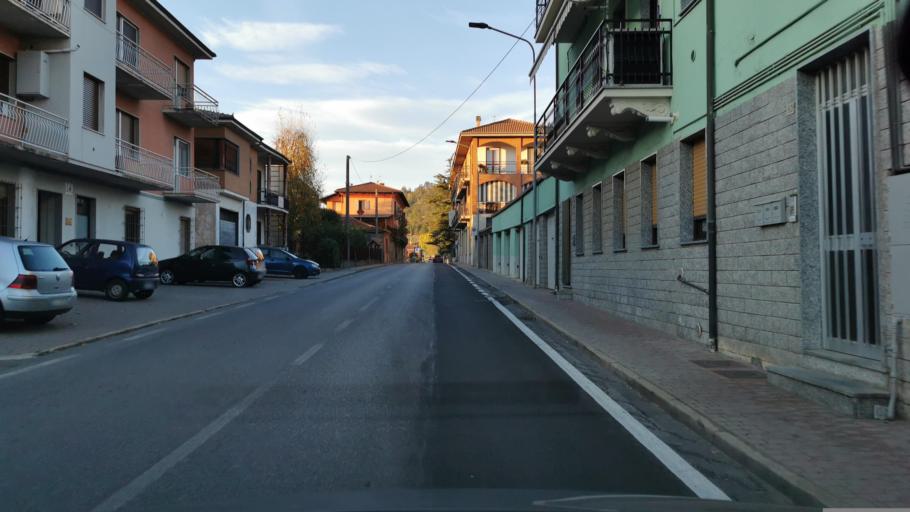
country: IT
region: Piedmont
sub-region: Provincia di Cuneo
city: Monchiero Borgonuovo
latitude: 44.5708
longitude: 7.9174
